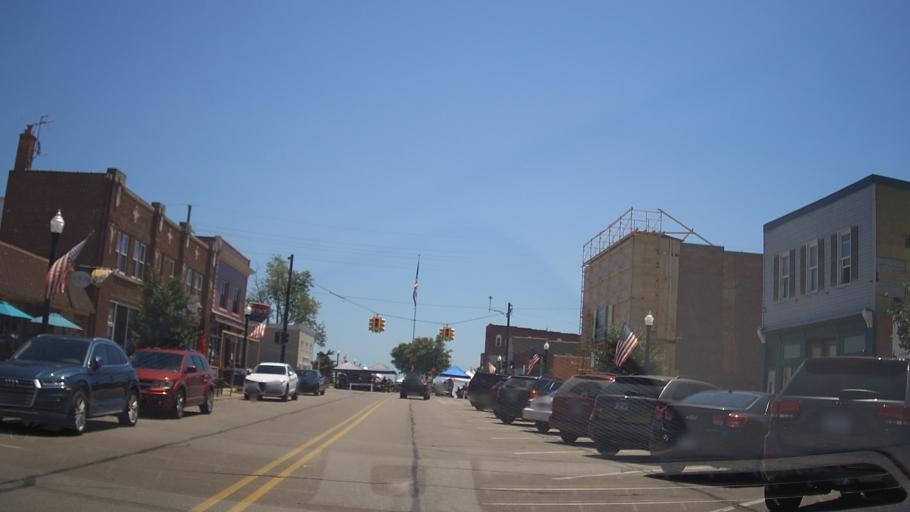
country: US
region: Michigan
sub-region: Macomb County
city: New Baltimore
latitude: 42.6801
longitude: -82.7355
